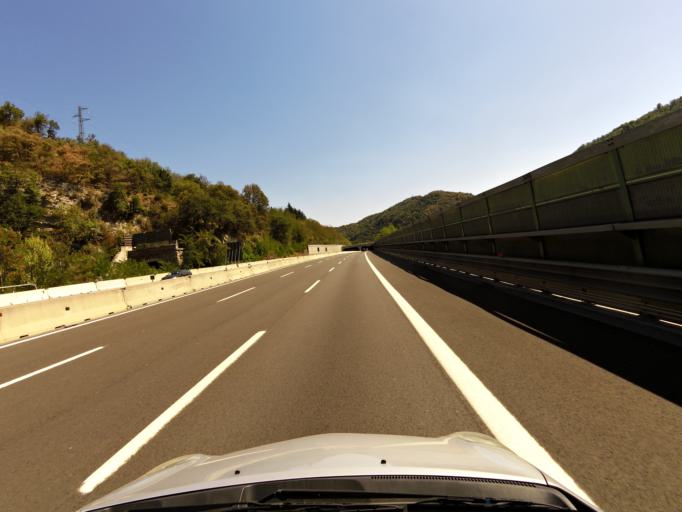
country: IT
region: Emilia-Romagna
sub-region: Provincia di Bologna
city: Vado
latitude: 44.2972
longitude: 11.2304
